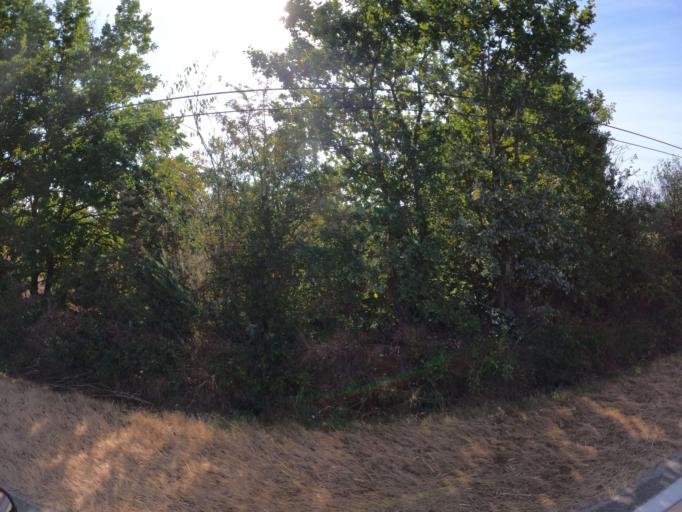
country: FR
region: Pays de la Loire
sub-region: Departement de la Vendee
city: Falleron
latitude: 46.8595
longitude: -1.7134
